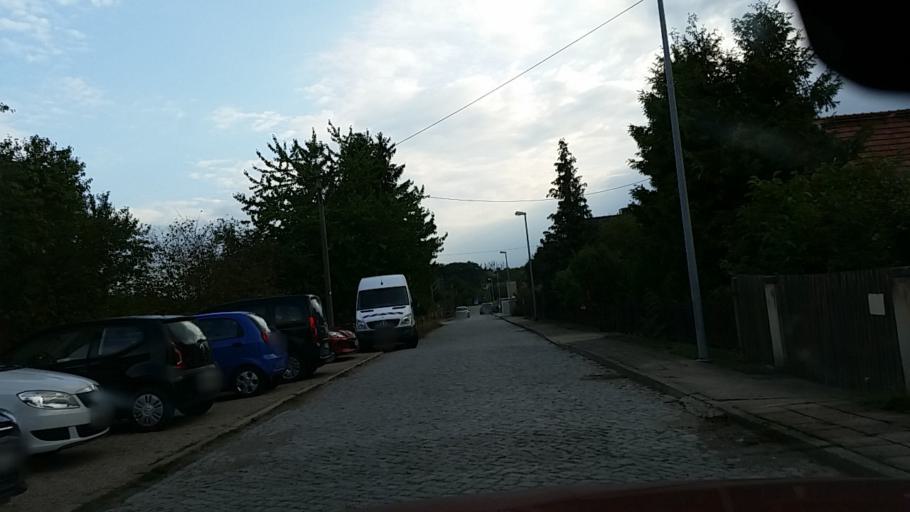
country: DE
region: Thuringia
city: Beichlingen
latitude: 51.2327
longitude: 11.2540
